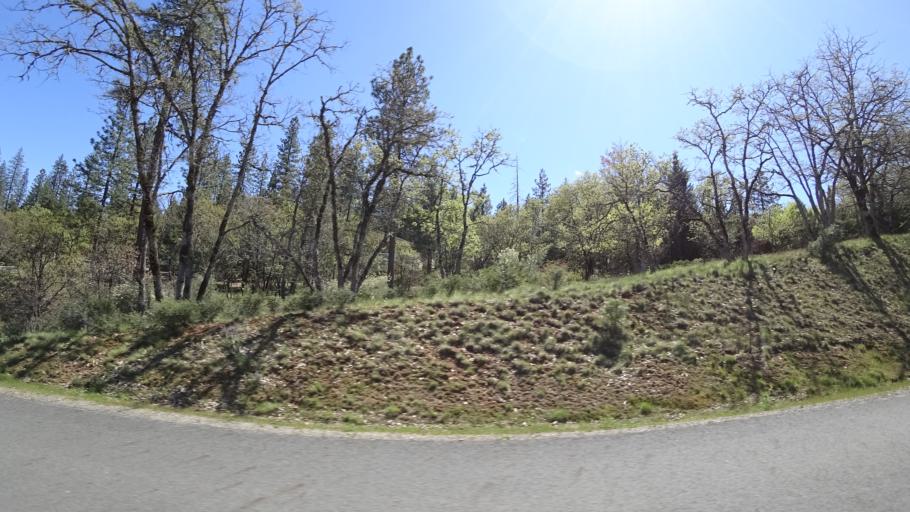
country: US
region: California
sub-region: Trinity County
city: Weaverville
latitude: 40.7346
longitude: -122.9566
